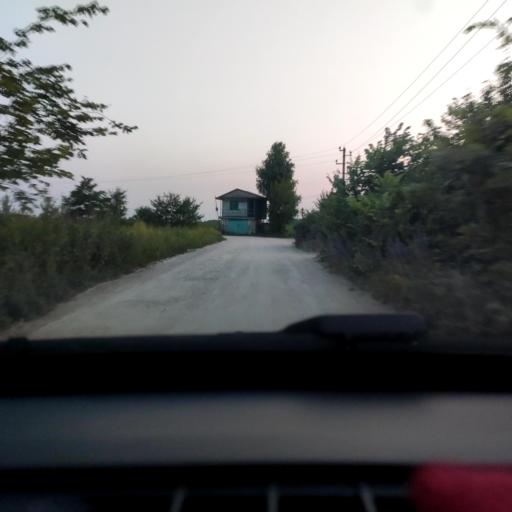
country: RU
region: Voronezj
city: Podgornoye
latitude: 51.8613
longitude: 39.1065
